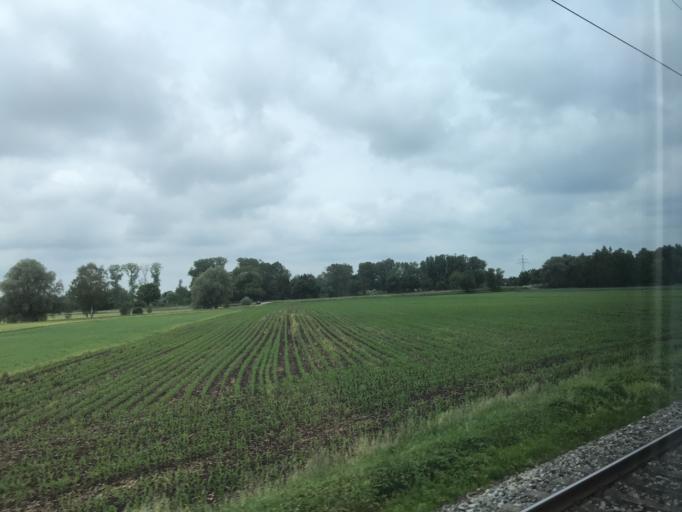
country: DE
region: Bavaria
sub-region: Swabia
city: Burgau
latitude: 48.4517
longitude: 10.4105
